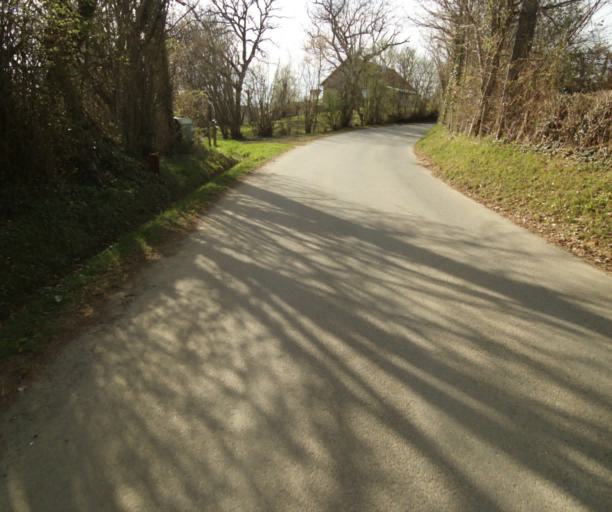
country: FR
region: Limousin
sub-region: Departement de la Correze
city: Naves
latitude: 45.3053
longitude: 1.7364
